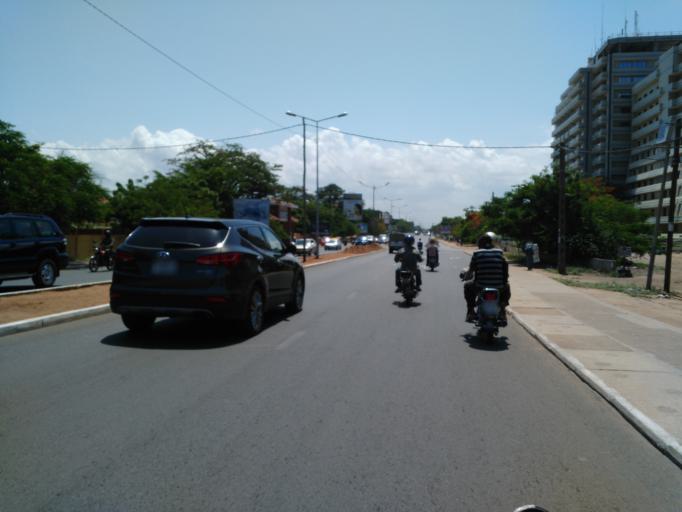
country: TG
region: Maritime
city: Lome
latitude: 6.1529
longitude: 1.2291
